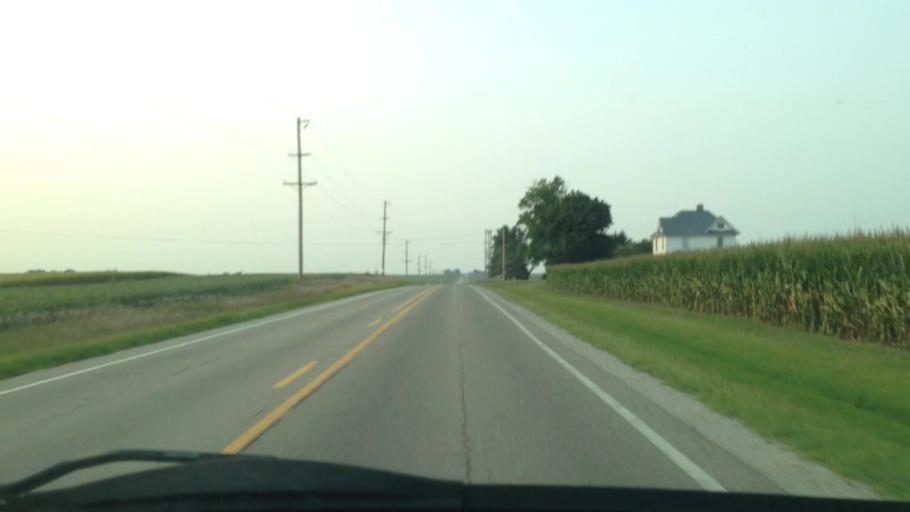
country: US
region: Iowa
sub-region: Iowa County
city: Marengo
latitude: 41.9403
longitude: -92.0849
